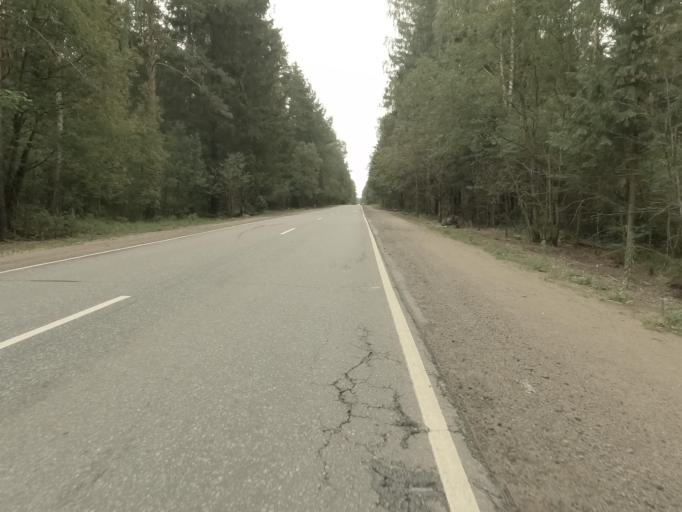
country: RU
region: Leningrad
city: Koltushi
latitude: 59.8952
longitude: 30.7502
